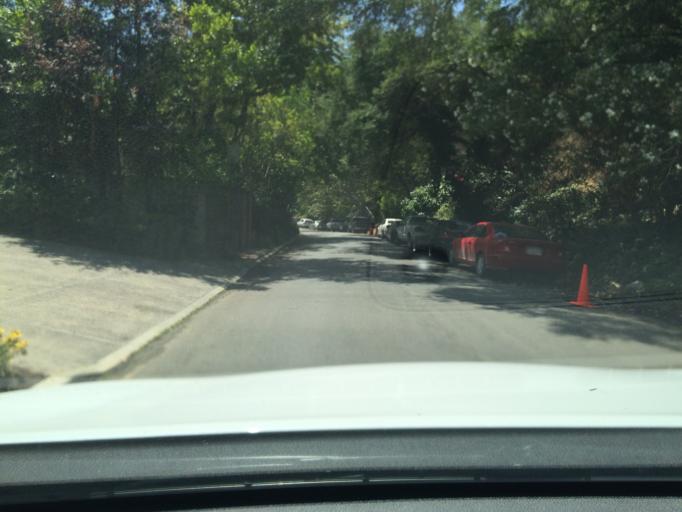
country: US
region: California
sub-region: Los Angeles County
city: Sherman Oaks
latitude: 34.1028
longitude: -118.4548
